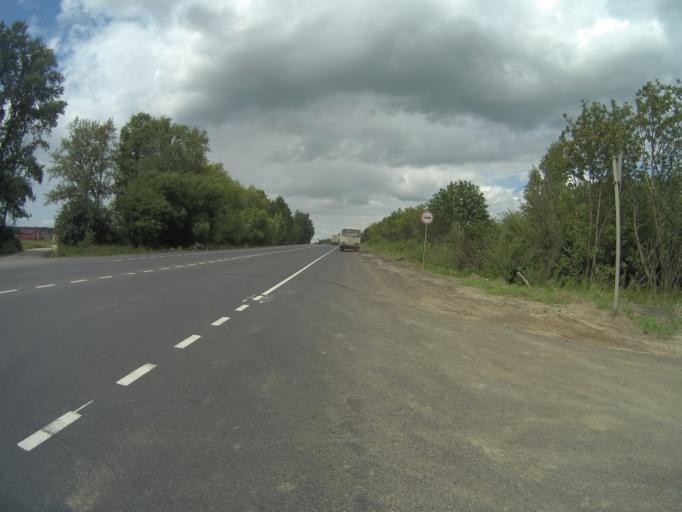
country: RU
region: Vladimir
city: Bogolyubovo
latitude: 56.1982
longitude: 40.4461
